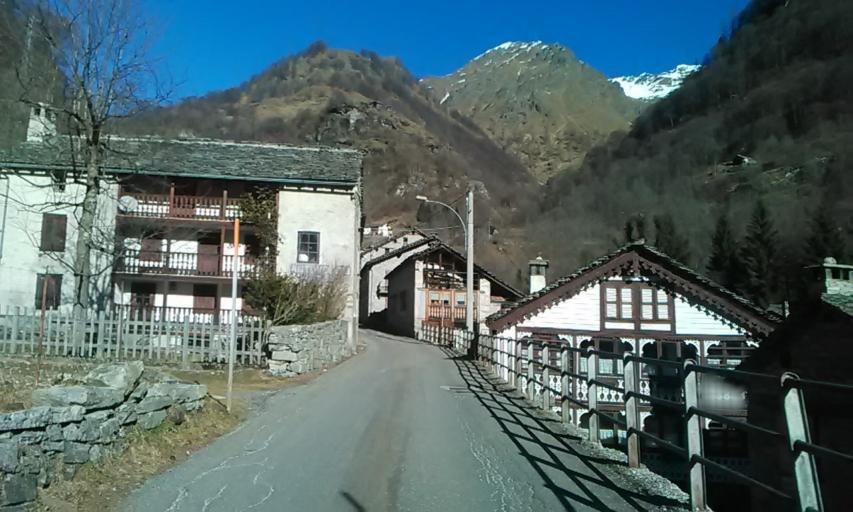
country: IT
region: Piedmont
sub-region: Provincia di Vercelli
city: Carcoforo
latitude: 45.8874
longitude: 8.0668
